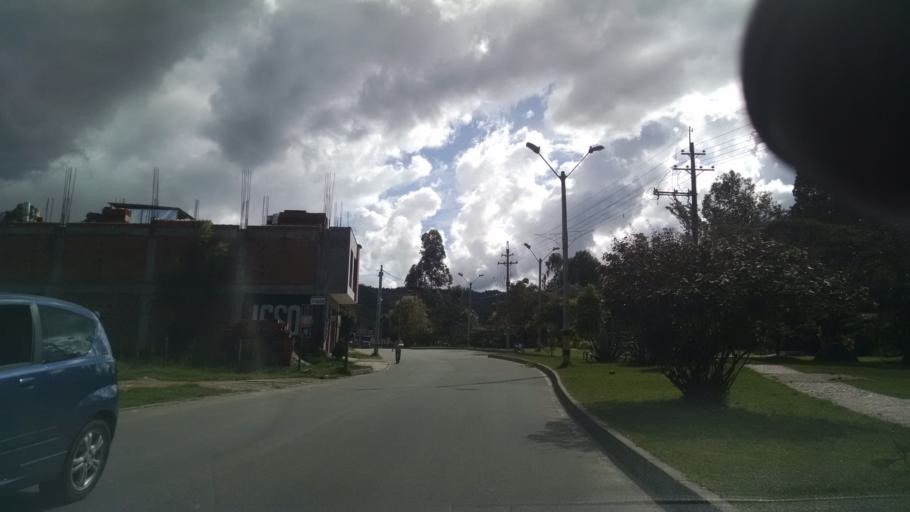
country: CO
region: Antioquia
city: El Retiro
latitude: 6.0632
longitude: -75.5026
